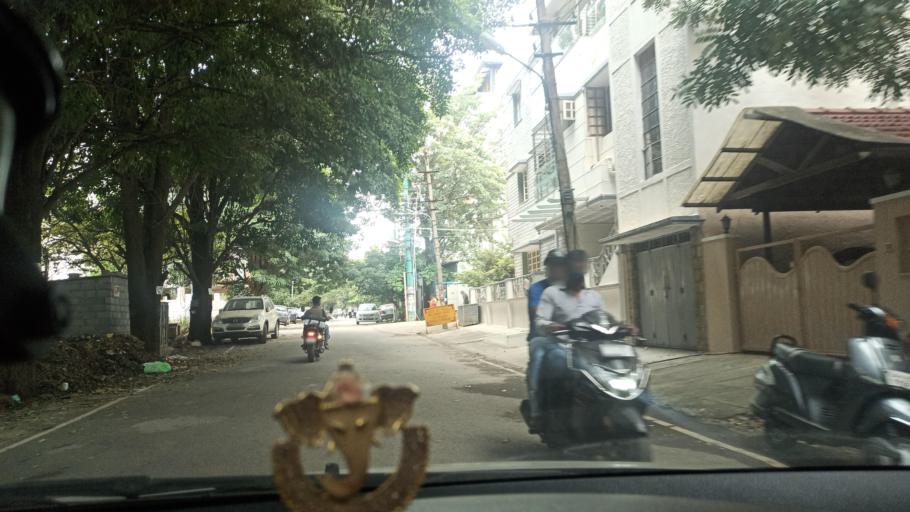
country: IN
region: Karnataka
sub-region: Bangalore Urban
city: Bangalore
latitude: 12.9167
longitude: 77.6471
